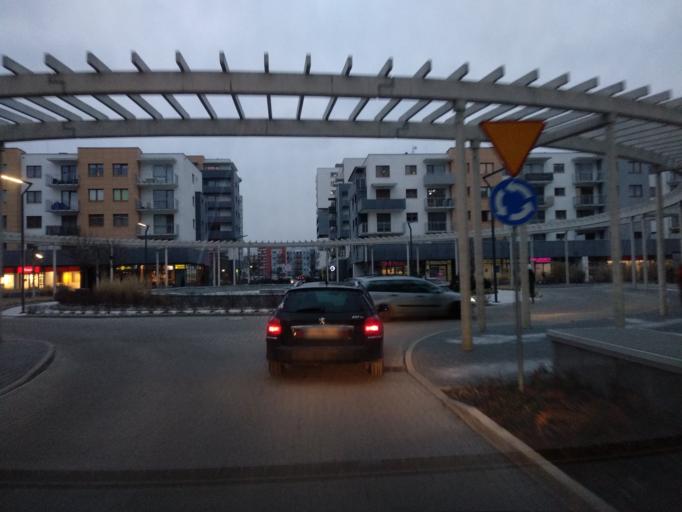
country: PL
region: Lower Silesian Voivodeship
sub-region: Powiat wroclawski
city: Wroclaw
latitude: 51.1267
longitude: 16.9667
